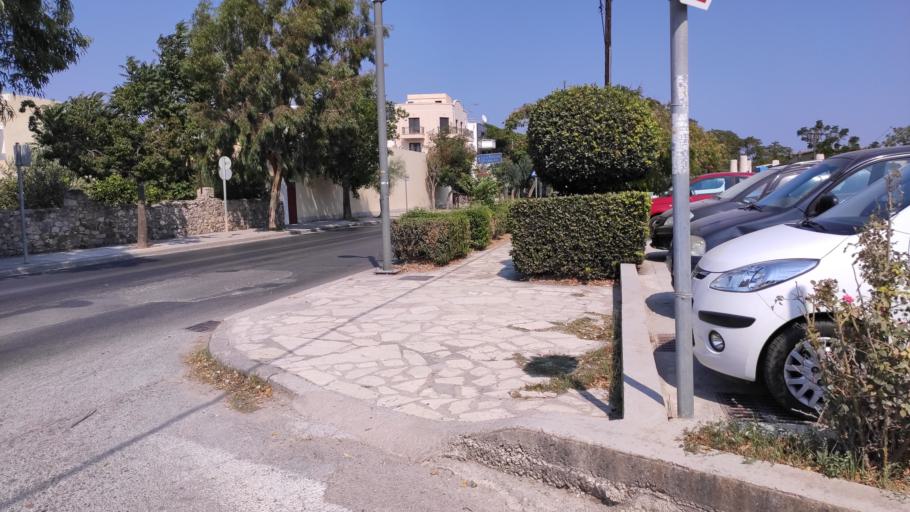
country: GR
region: South Aegean
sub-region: Nomos Dodekanisou
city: Kos
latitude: 36.8903
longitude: 27.2874
